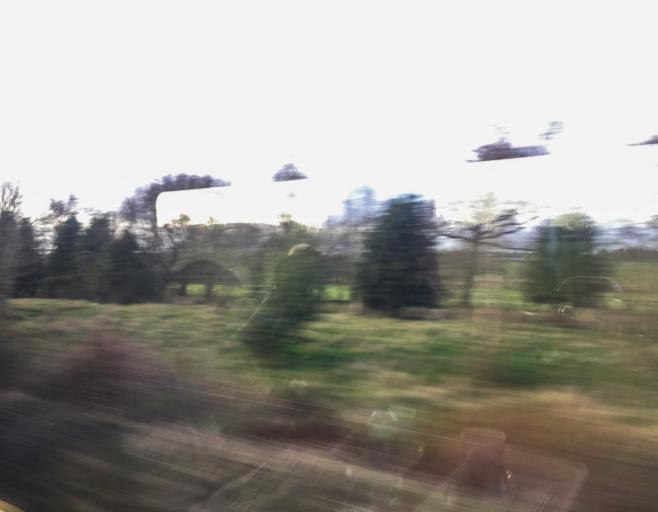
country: GB
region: Scotland
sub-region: Dumfries and Galloway
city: Gretna
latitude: 55.0213
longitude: -3.1126
